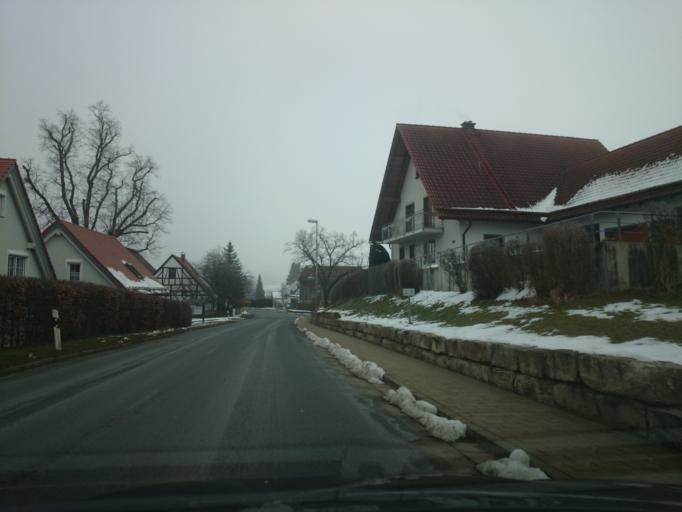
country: DE
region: Bavaria
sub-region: Regierungsbezirk Mittelfranken
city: Thalmassing
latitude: 49.1112
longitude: 11.2769
